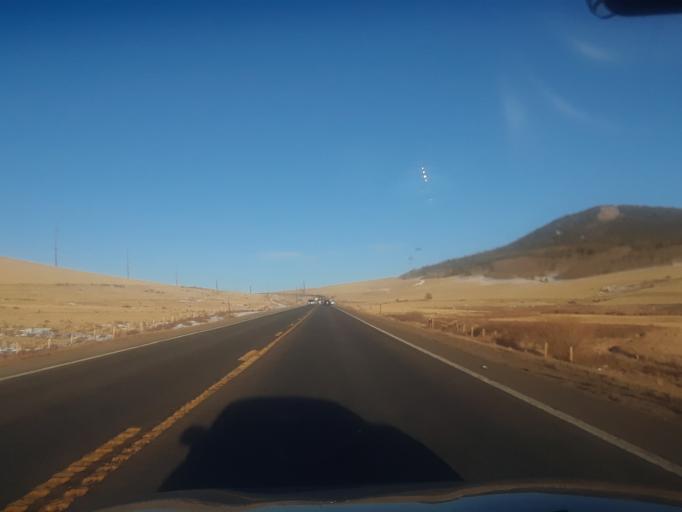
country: US
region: Colorado
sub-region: Park County
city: Fairplay
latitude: 39.2753
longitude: -105.9361
